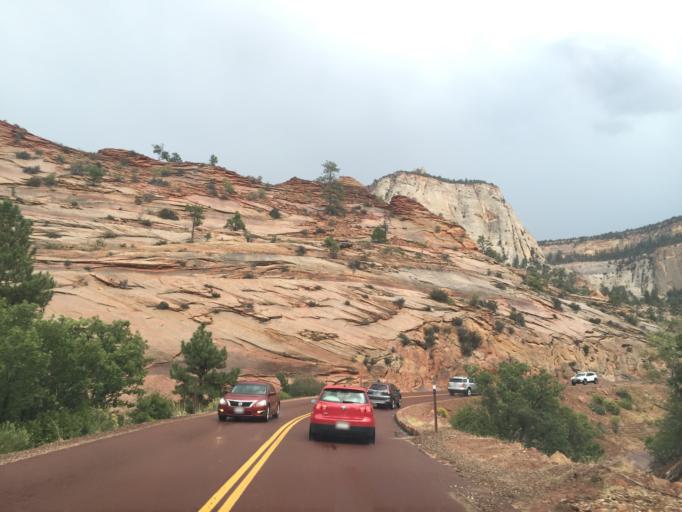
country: US
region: Utah
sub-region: Washington County
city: Hildale
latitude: 37.2239
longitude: -112.9004
